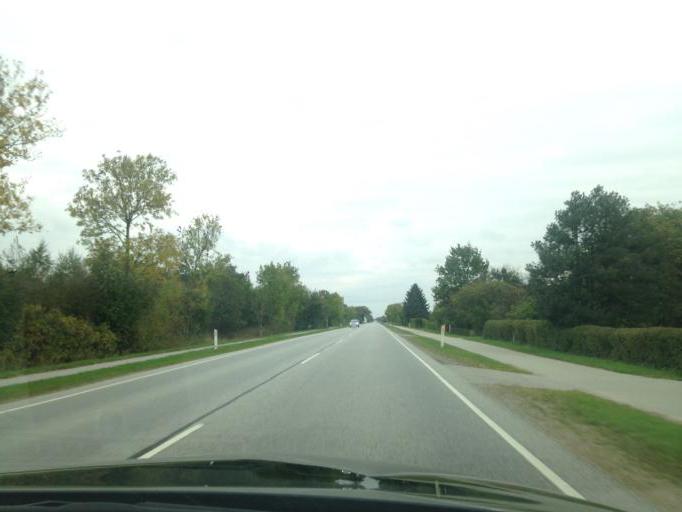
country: DK
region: South Denmark
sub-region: Haderslev Kommune
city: Haderslev
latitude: 55.2775
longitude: 9.4978
